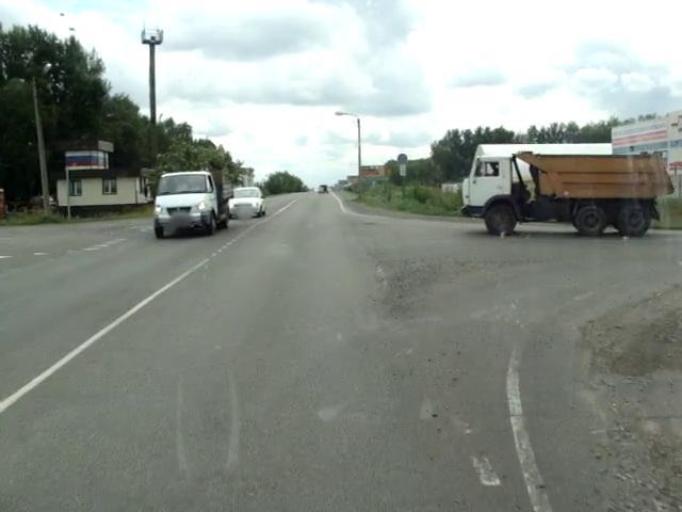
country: RU
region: Altai Krai
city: Zarya
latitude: 52.5752
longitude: 85.1804
